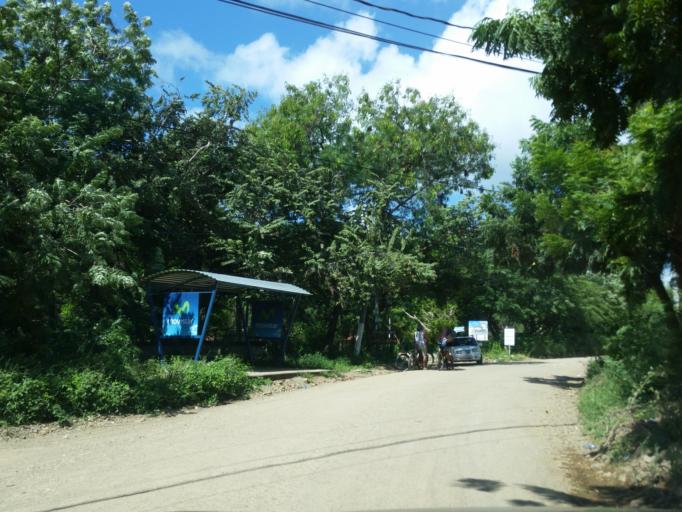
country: NI
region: Rivas
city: San Juan del Sur
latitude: 11.2612
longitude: -85.8745
